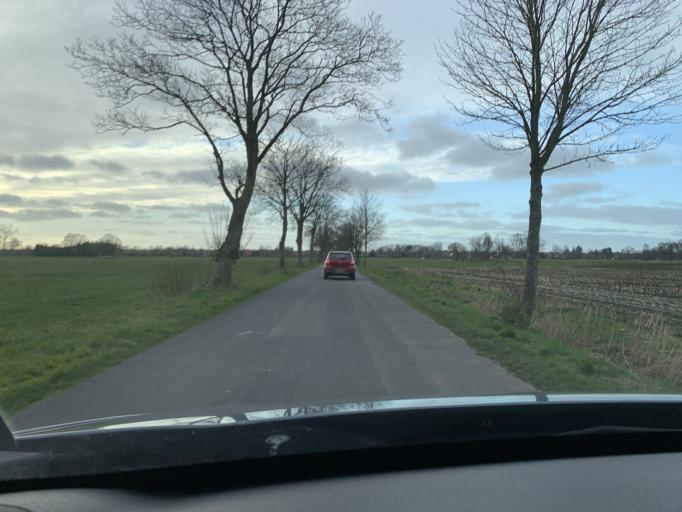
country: DE
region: Lower Saxony
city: Schwerinsdorf
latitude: 53.2674
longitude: 7.7052
